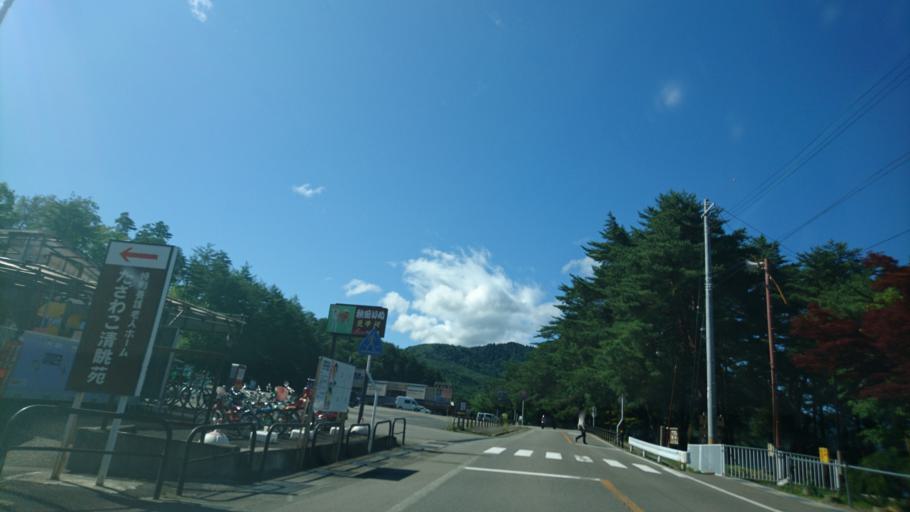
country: JP
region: Akita
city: Kakunodatemachi
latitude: 39.7322
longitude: 140.6990
